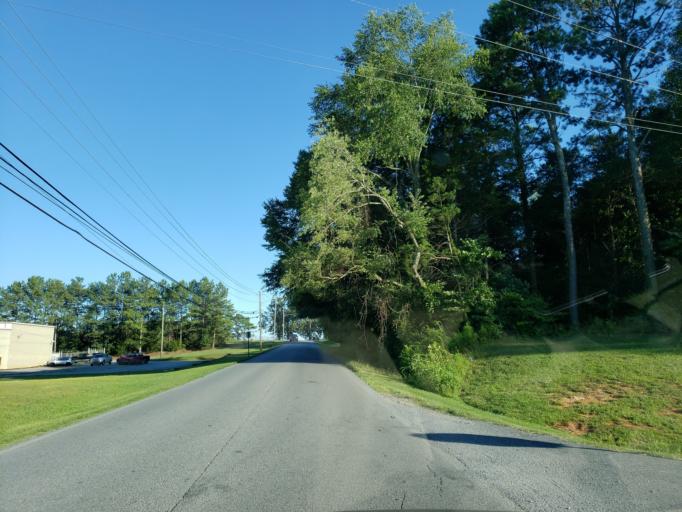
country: US
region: Georgia
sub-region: Polk County
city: Rockmart
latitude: 34.0157
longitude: -85.0652
